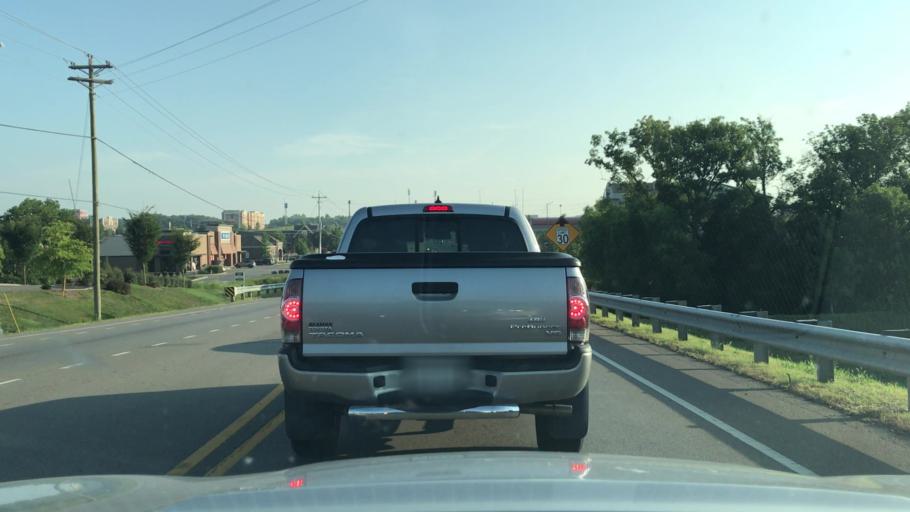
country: US
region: Tennessee
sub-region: Wilson County
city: Mount Juliet
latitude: 36.1616
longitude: -86.5152
